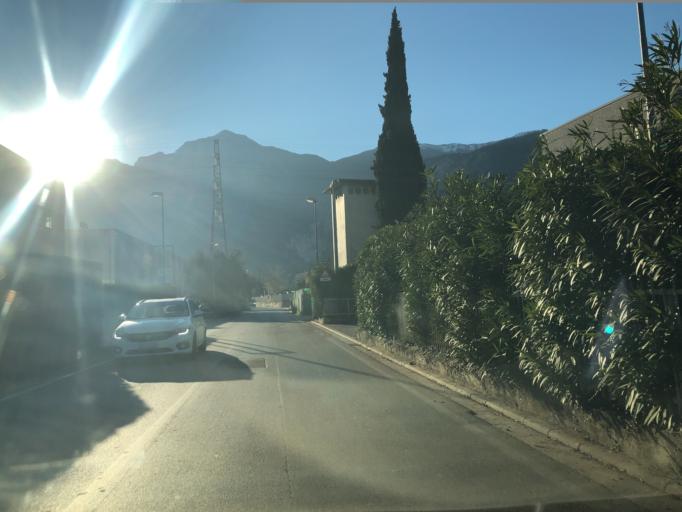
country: IT
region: Trentino-Alto Adige
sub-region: Provincia di Trento
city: Arco
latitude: 45.9148
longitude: 10.8608
